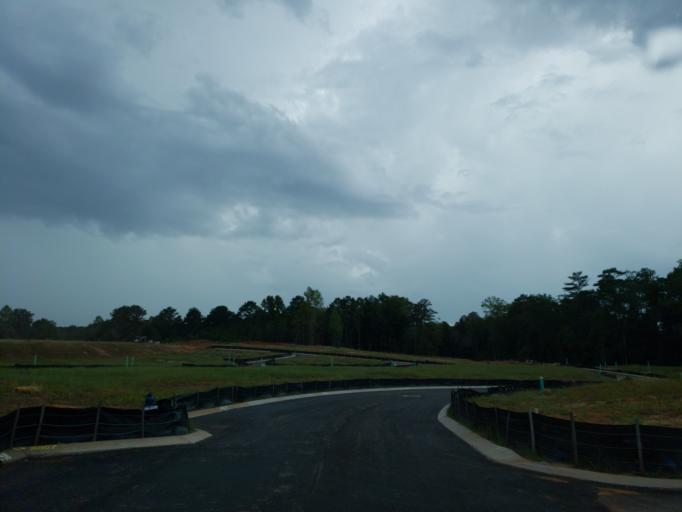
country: US
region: Georgia
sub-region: Cherokee County
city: Woodstock
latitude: 34.0929
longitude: -84.5241
